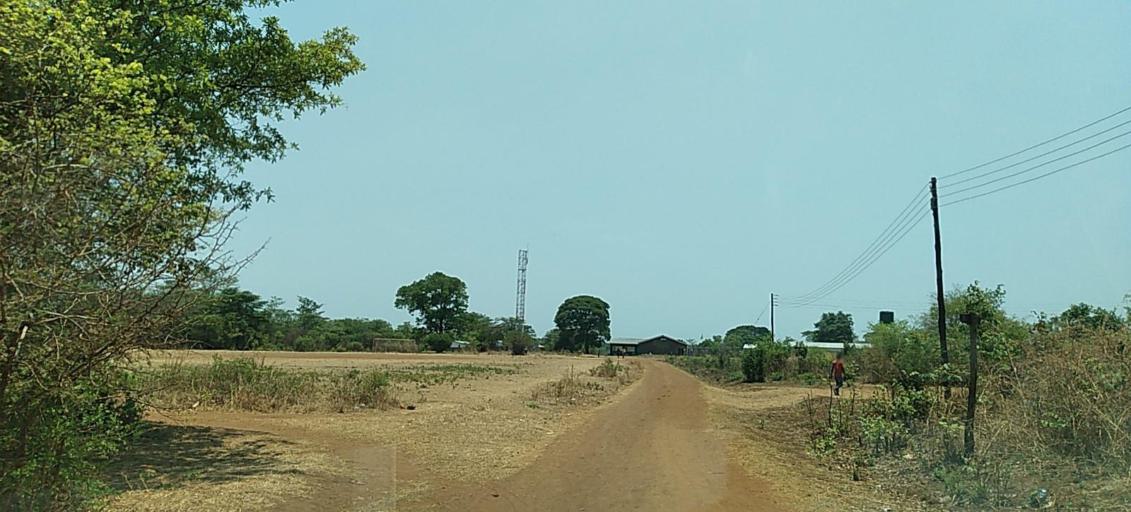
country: ZM
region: Copperbelt
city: Mpongwe
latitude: -13.8356
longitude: 27.8378
